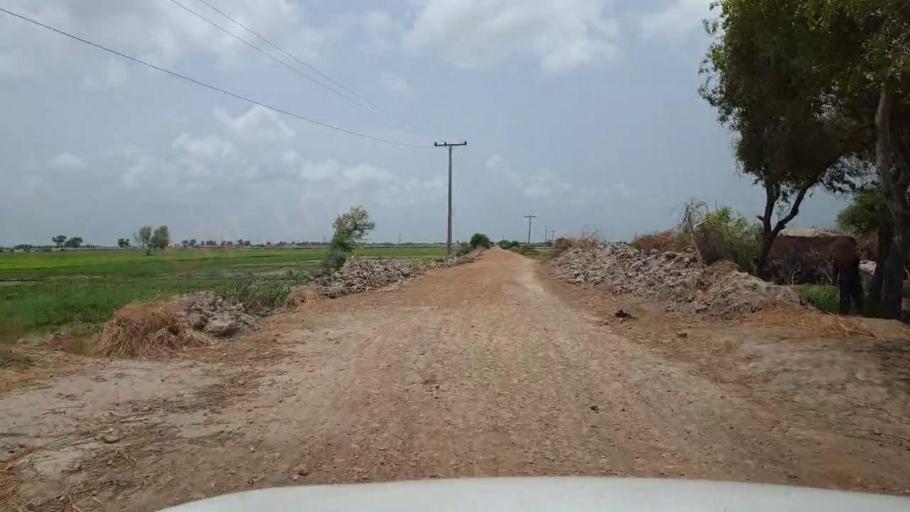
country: PK
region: Sindh
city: Kario
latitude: 24.7605
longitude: 68.4577
